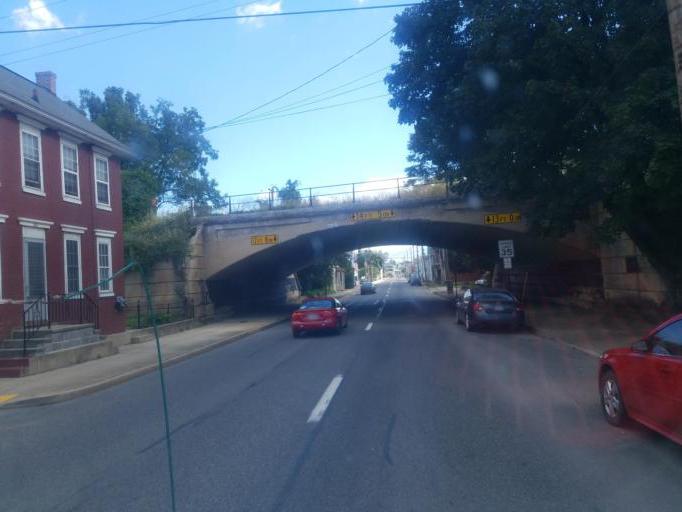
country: US
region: Pennsylvania
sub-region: Franklin County
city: Chambersburg
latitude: 39.9352
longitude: -77.6559
